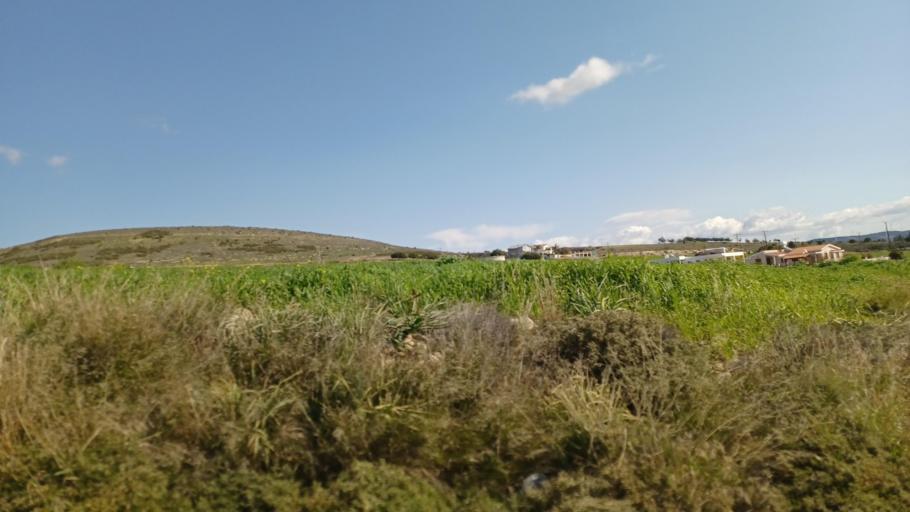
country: CY
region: Pafos
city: Mesogi
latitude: 34.7486
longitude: 32.5342
